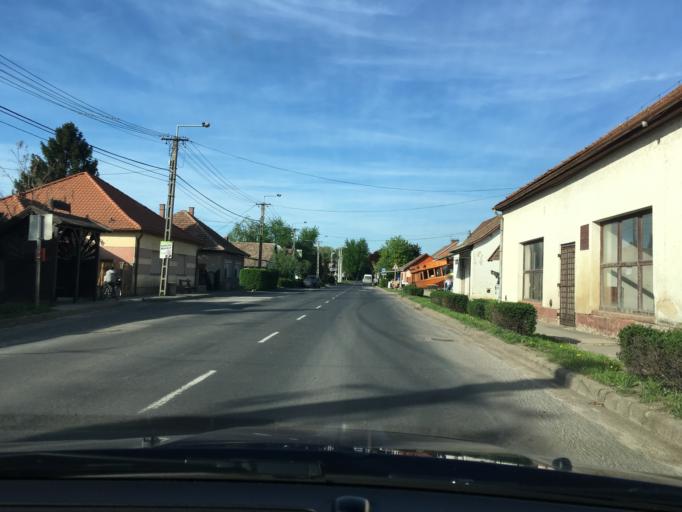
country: HU
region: Bekes
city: Korostarcsa
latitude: 46.8799
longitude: 21.0264
